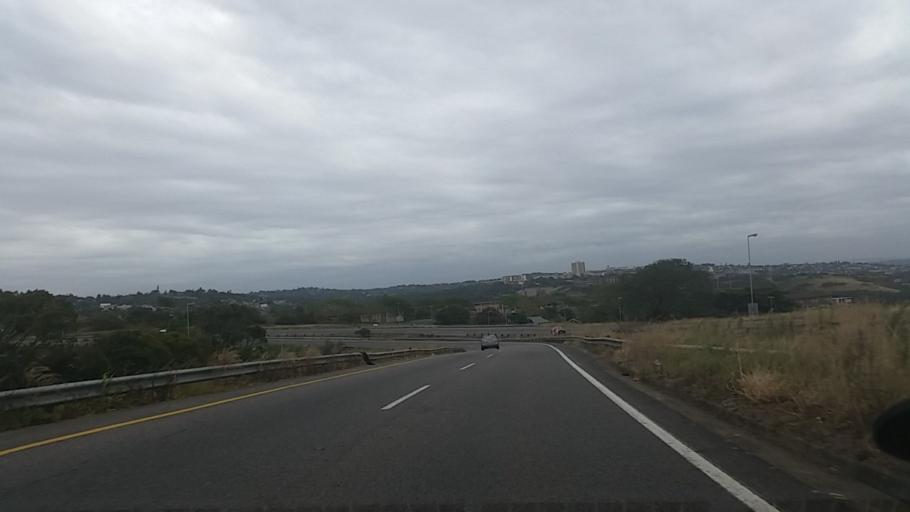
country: ZA
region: KwaZulu-Natal
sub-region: eThekwini Metropolitan Municipality
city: Berea
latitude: -29.8298
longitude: 30.9591
